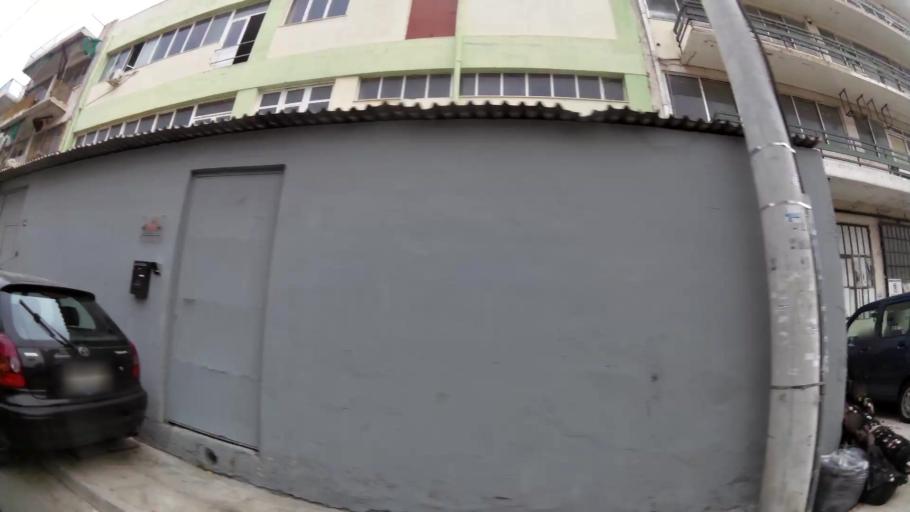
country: GR
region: Attica
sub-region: Nomos Piraios
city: Agios Ioannis Rentis
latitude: 37.9617
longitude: 23.6606
